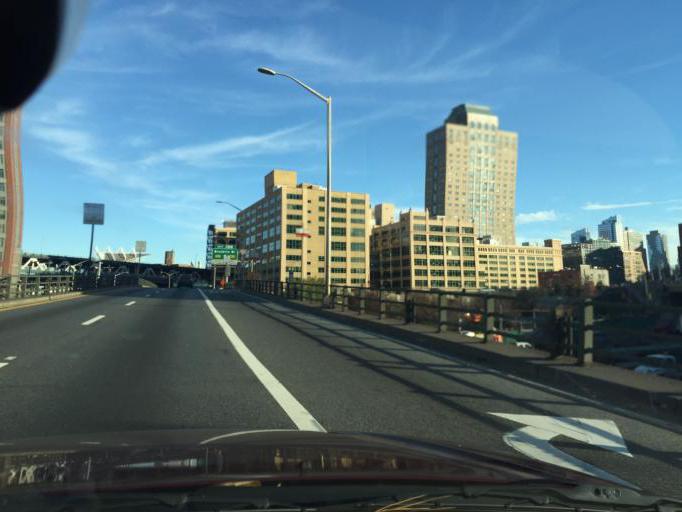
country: US
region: New York
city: New York City
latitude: 40.7016
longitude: -73.9906
